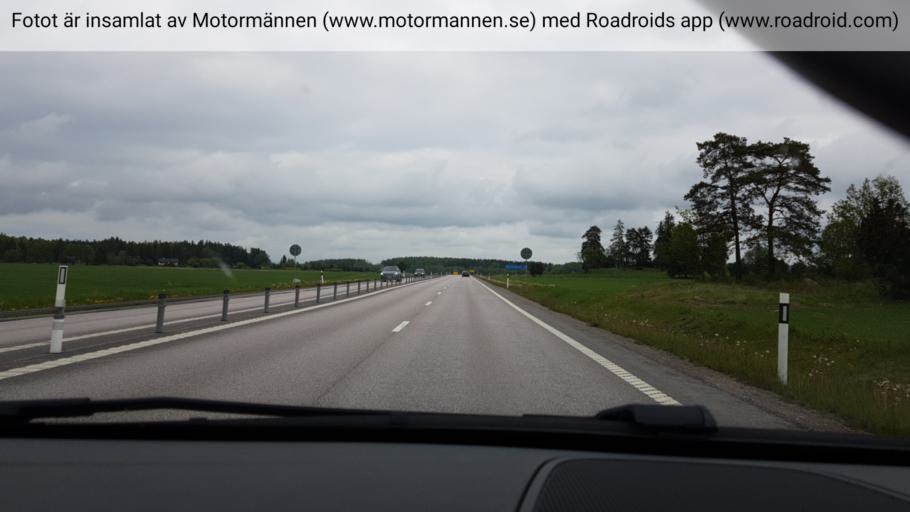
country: SE
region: Uppsala
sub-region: Uppsala Kommun
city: Vattholma
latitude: 59.9528
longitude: 17.8730
